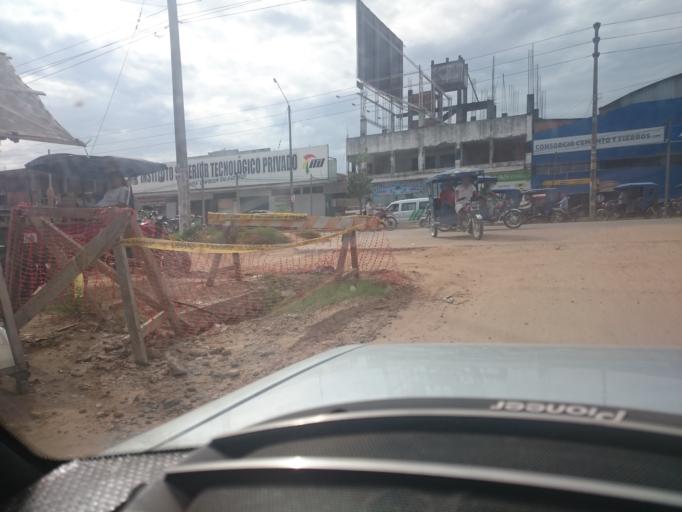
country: PE
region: Ucayali
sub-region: Provincia de Coronel Portillo
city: Pucallpa
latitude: -8.3839
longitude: -74.5455
